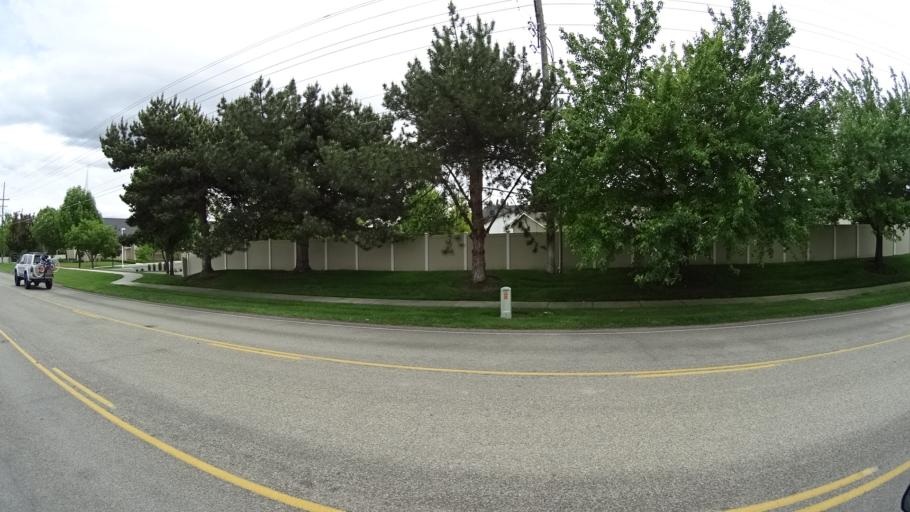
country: US
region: Idaho
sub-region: Ada County
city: Meridian
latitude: 43.6340
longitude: -116.4255
